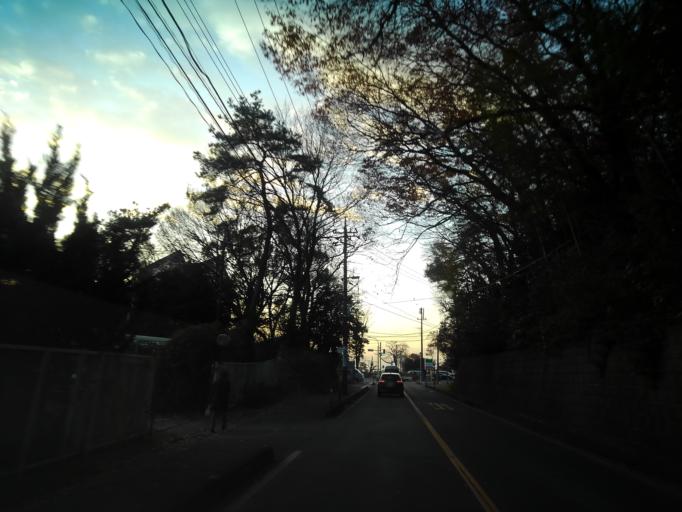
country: JP
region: Tokyo
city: Higashimurayama-shi
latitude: 35.7703
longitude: 139.4380
